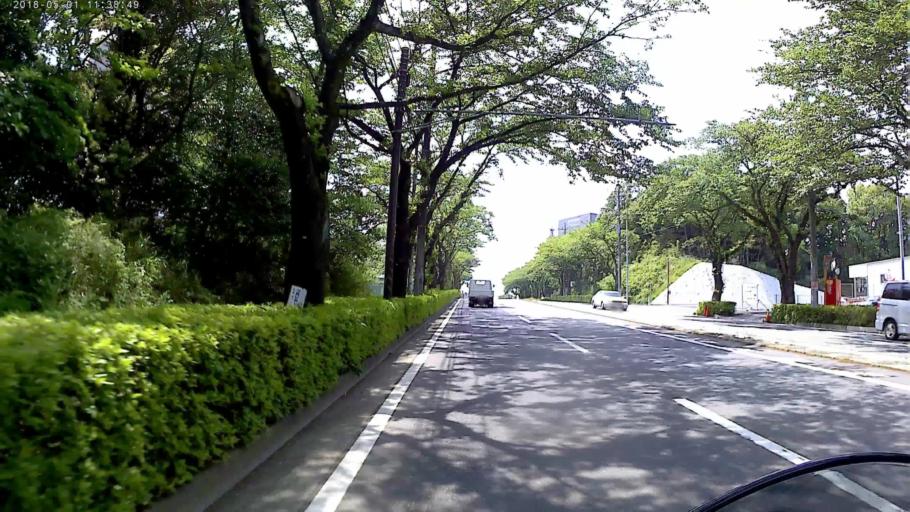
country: JP
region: Kanagawa
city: Minami-rinkan
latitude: 35.5067
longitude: 139.4905
